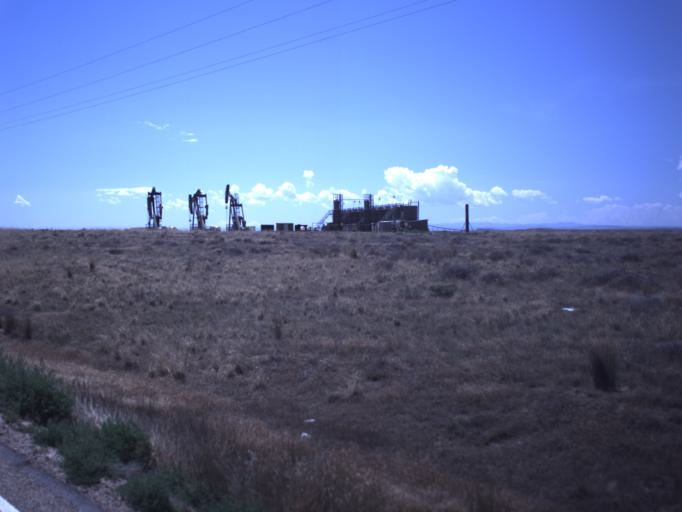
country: US
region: Utah
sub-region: Uintah County
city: Naples
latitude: 40.1572
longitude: -109.6643
